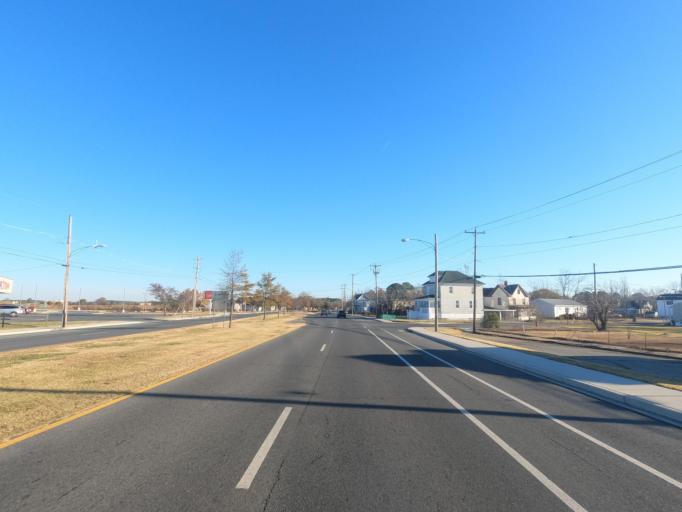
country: US
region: Maryland
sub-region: Somerset County
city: Crisfield
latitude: 37.9838
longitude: -75.8539
